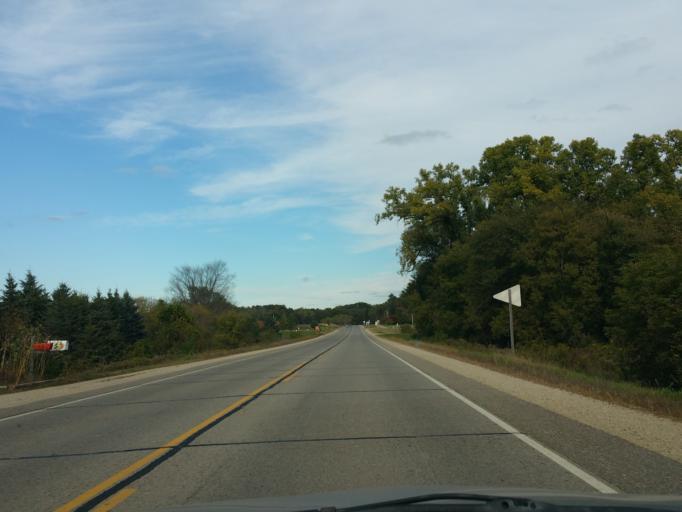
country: US
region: Wisconsin
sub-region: Pierce County
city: River Falls
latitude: 44.8280
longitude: -92.6337
